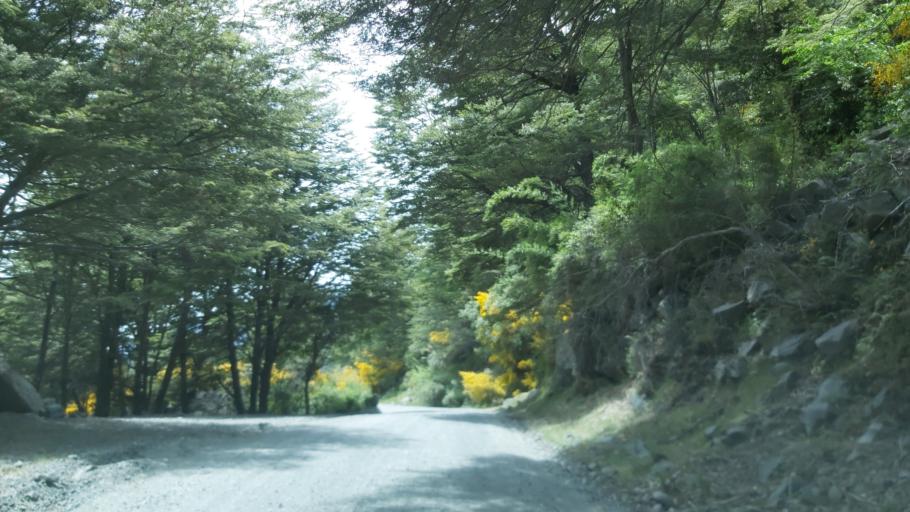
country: AR
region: Neuquen
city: Las Ovejas
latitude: -37.3971
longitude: -71.4487
